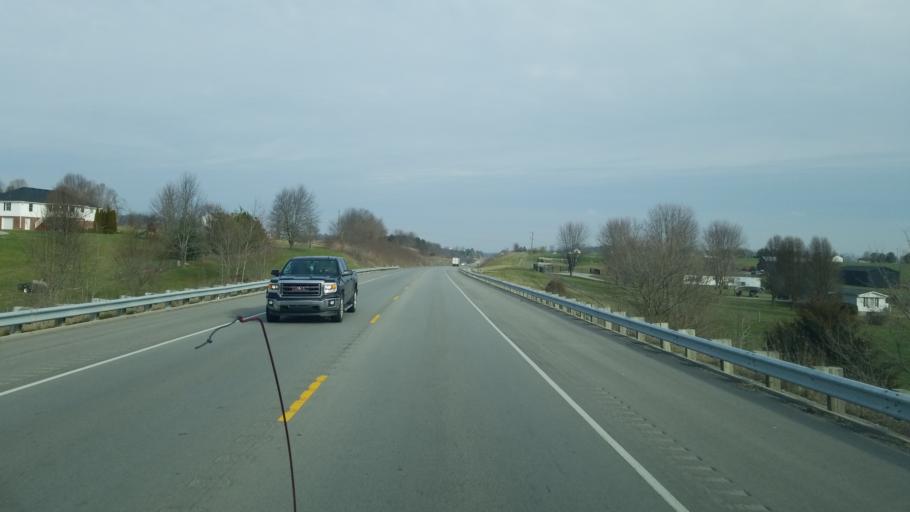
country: US
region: Kentucky
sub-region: Boyle County
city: Junction City
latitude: 37.5315
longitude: -84.8050
